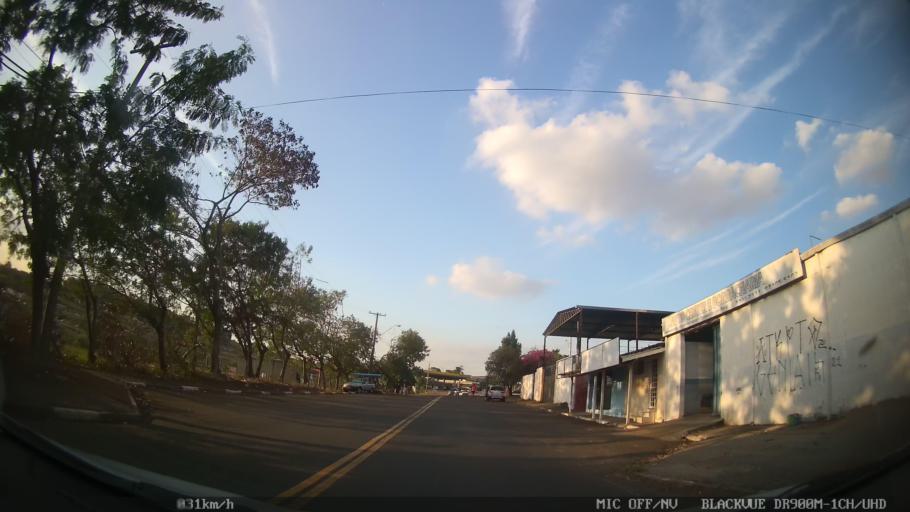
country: BR
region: Sao Paulo
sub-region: Hortolandia
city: Hortolandia
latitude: -22.8892
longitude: -47.1454
